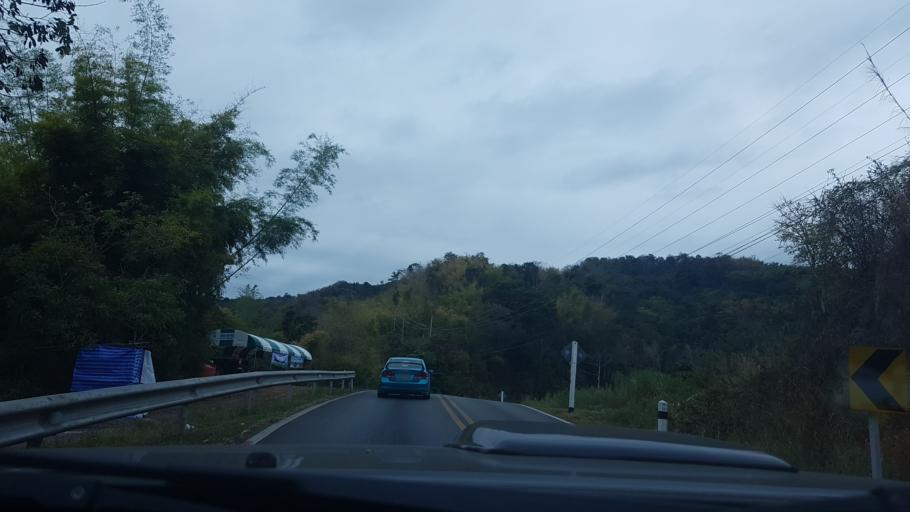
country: TH
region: Phetchabun
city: Khao Kho
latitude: 16.5478
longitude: 101.0370
